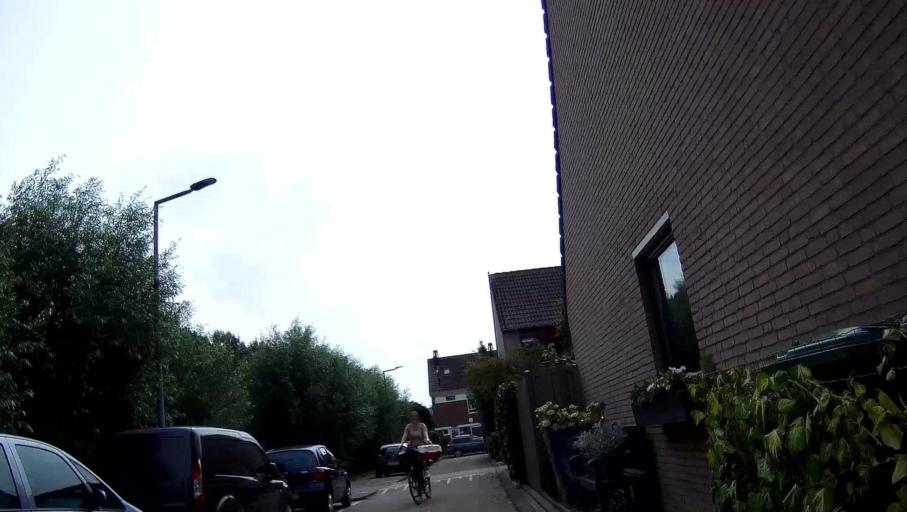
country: NL
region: South Holland
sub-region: Gemeente Rotterdam
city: Hoek van Holland
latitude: 51.9796
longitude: 4.1401
